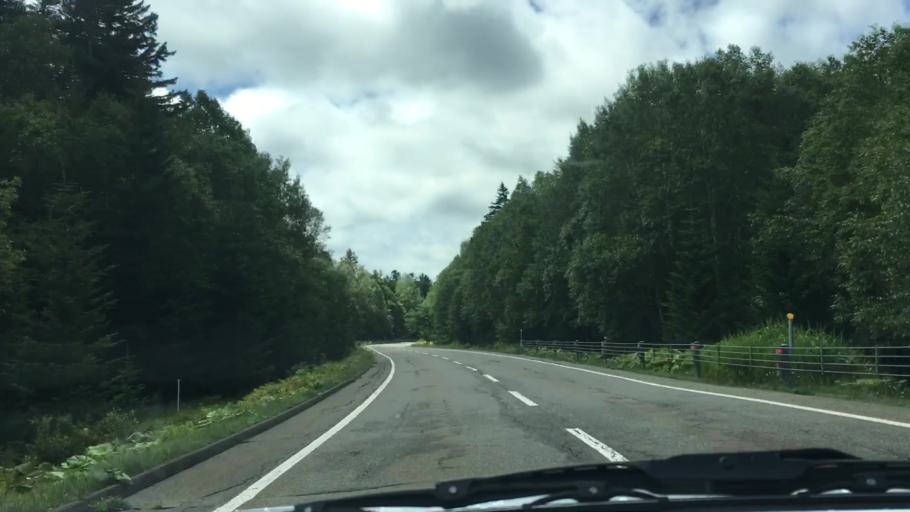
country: JP
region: Hokkaido
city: Kitami
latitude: 43.4160
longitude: 143.9743
